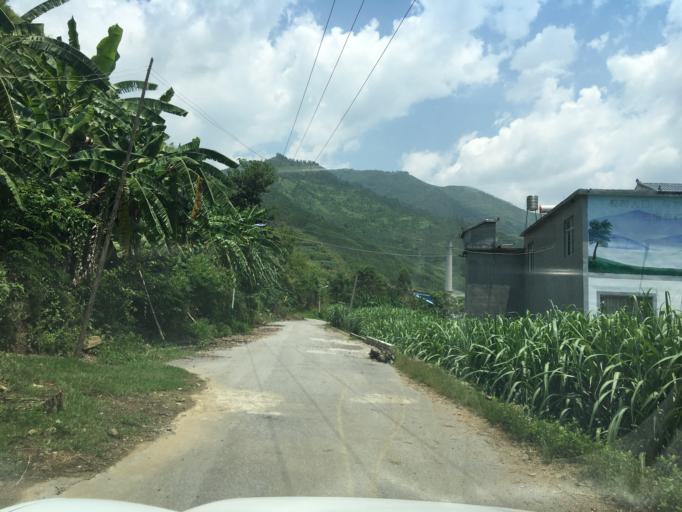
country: CN
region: Guangxi Zhuangzu Zizhiqu
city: Xinzhou
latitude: 24.9076
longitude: 105.4743
